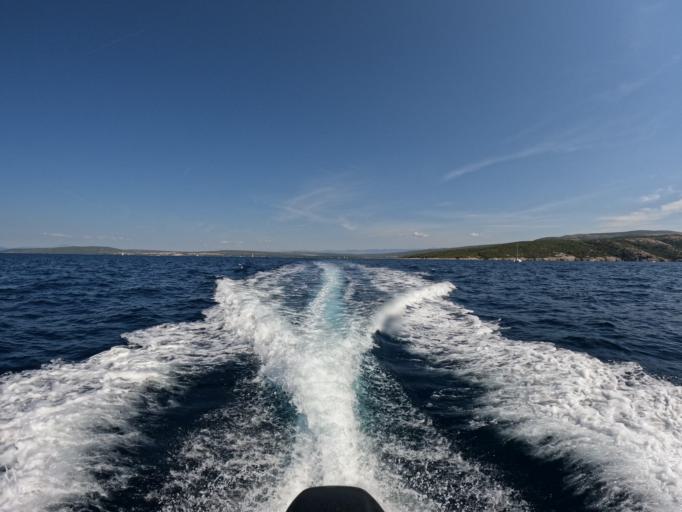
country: HR
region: Primorsko-Goranska
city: Punat
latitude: 44.9695
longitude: 14.6085
